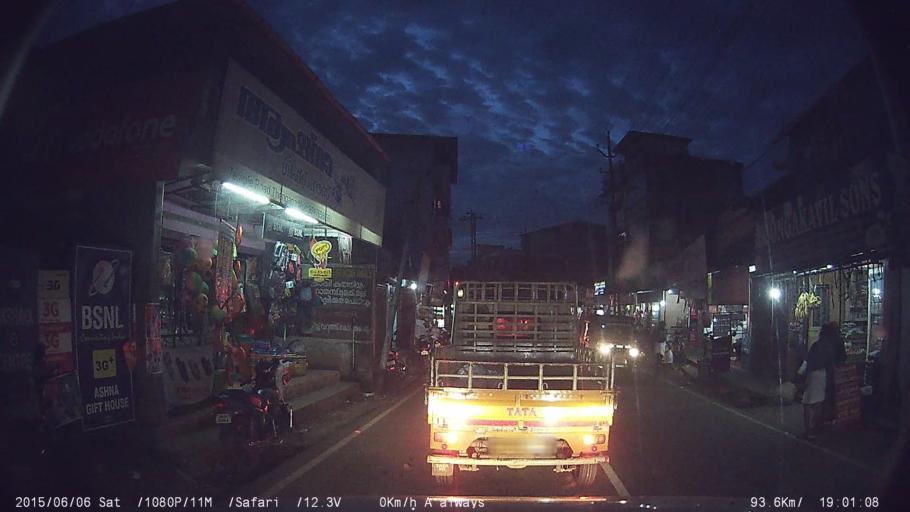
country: IN
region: Kerala
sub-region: Kottayam
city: Changanacheri
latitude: 9.4742
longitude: 76.5770
